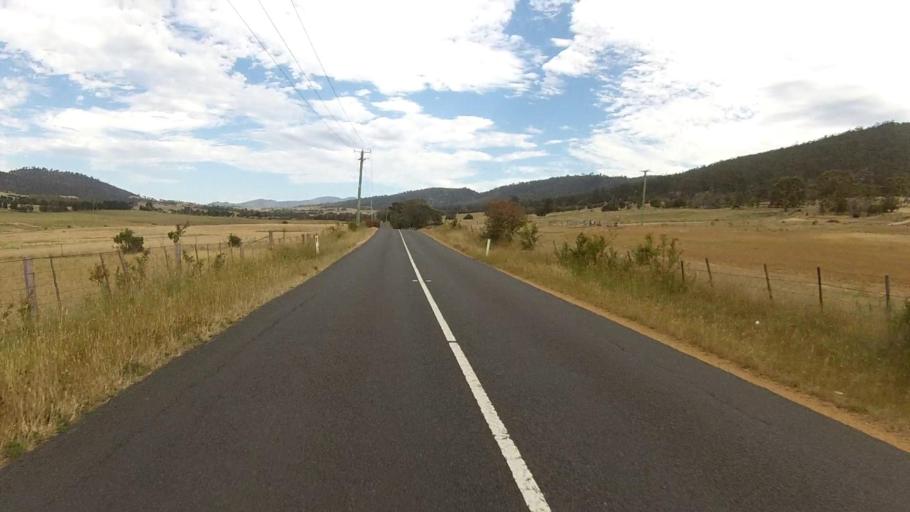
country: AU
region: Tasmania
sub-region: Clarence
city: Cambridge
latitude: -42.7285
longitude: 147.4000
